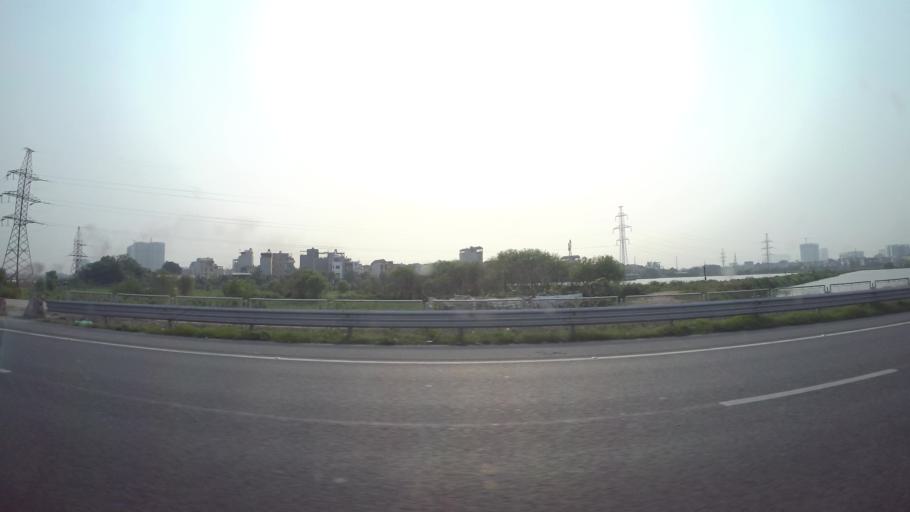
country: VN
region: Ha Noi
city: Van Dien
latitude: 20.9410
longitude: 105.8594
